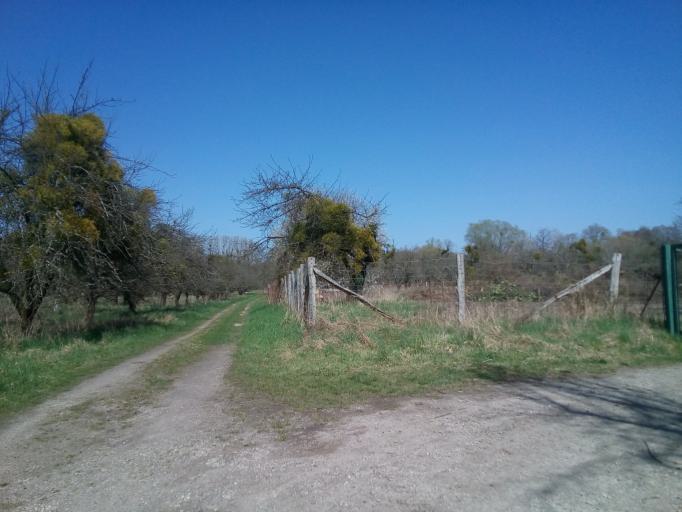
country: DE
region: Baden-Wuerttemberg
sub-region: Freiburg Region
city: Rheinau
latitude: 48.6627
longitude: 7.9112
